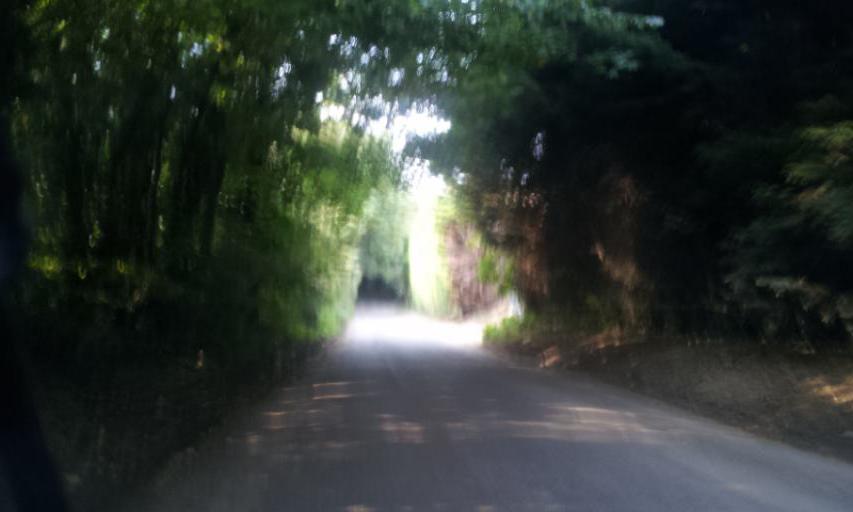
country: GB
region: England
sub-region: Kent
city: Yalding
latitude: 51.2372
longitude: 0.4232
